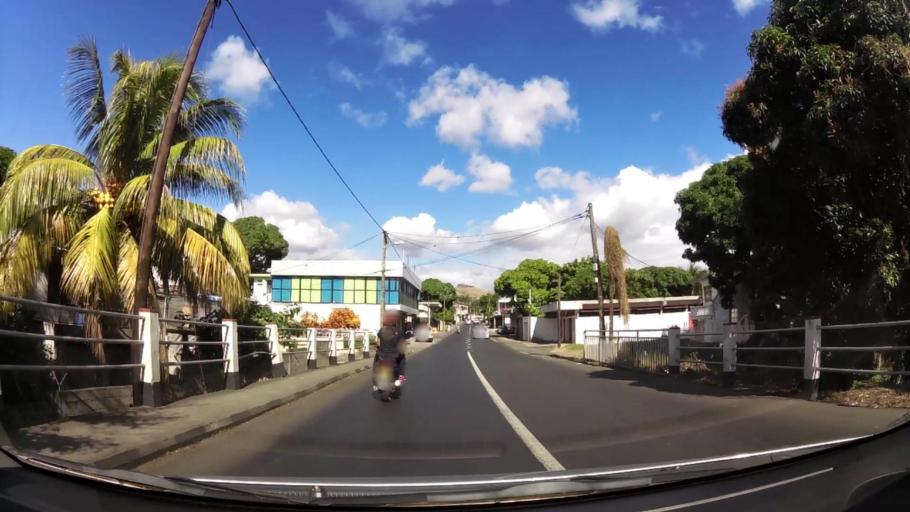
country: MU
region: Pamplemousses
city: Le Hochet
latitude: -20.1514
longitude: 57.5221
